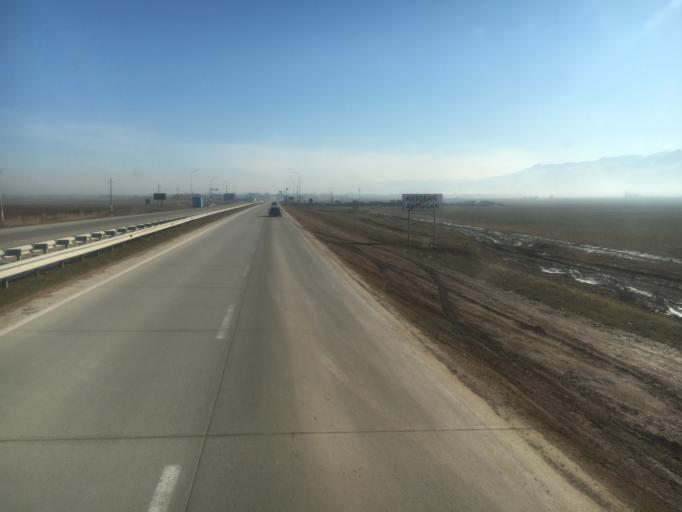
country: KZ
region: Zhambyl
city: Merke
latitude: 42.8759
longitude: 73.1171
